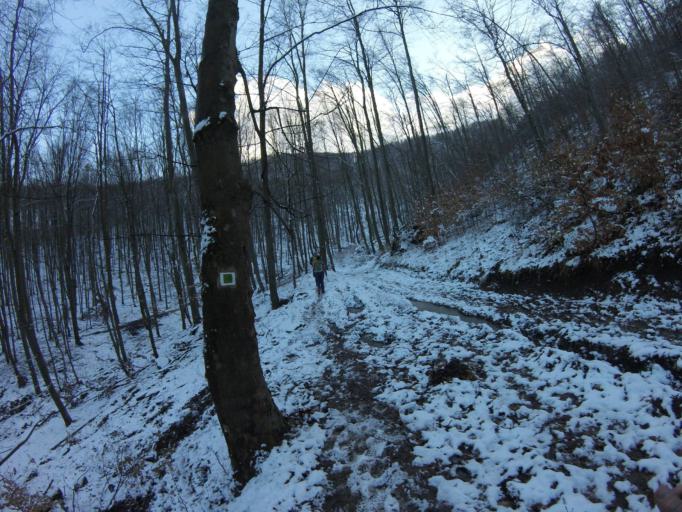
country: HU
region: Pest
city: Pilisszentkereszt
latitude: 47.7255
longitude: 18.8967
